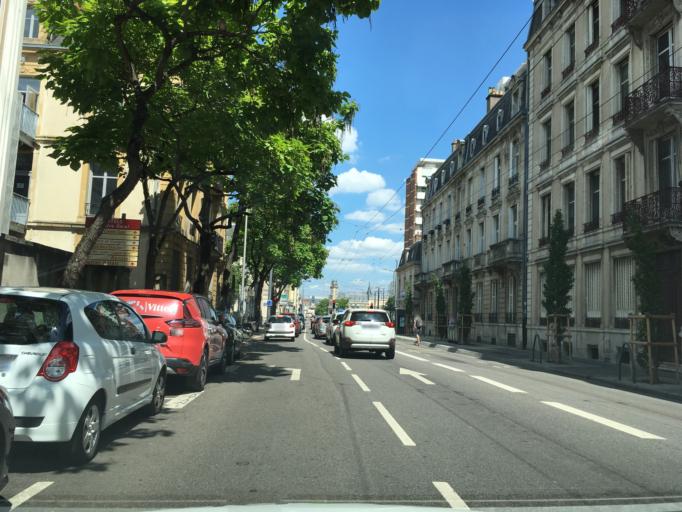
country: FR
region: Lorraine
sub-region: Departement de Meurthe-et-Moselle
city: Nancy
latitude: 48.6881
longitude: 6.1722
